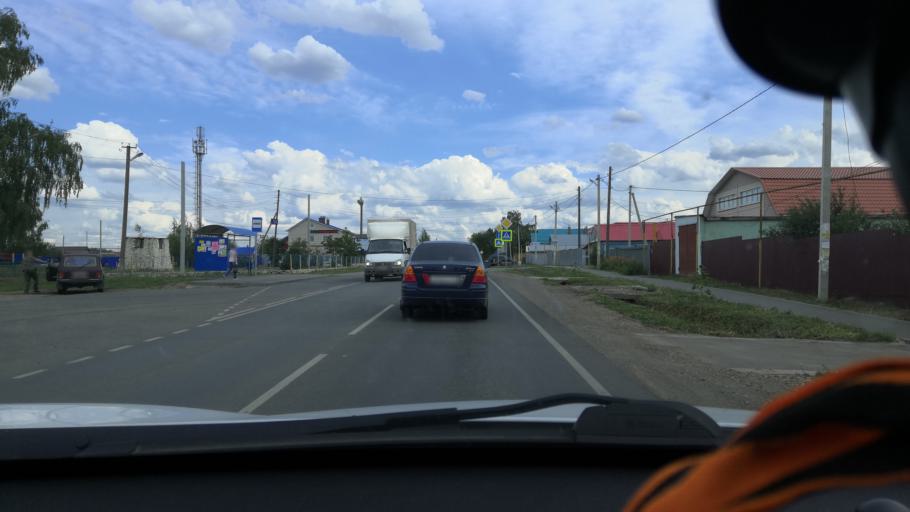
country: RU
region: Samara
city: Novosemeykino
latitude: 53.3762
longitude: 50.3464
